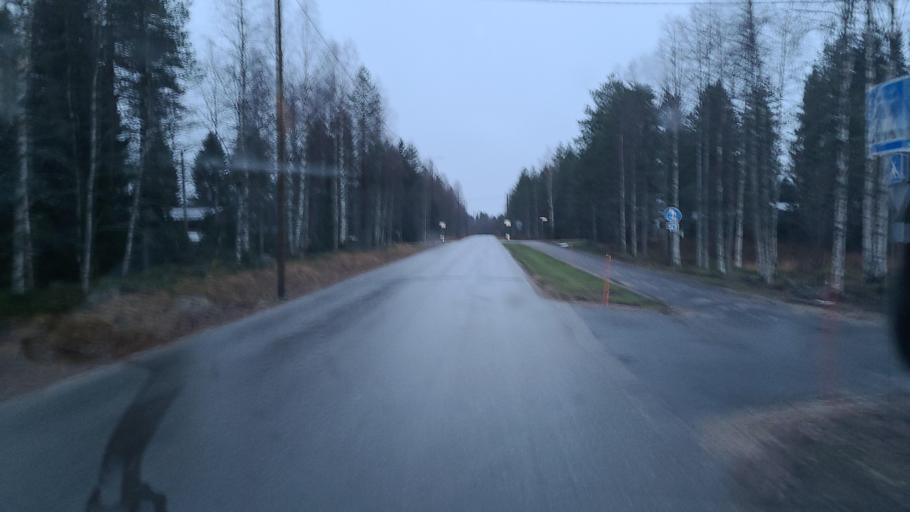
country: FI
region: Lapland
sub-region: Rovaniemi
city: Ranua
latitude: 65.9283
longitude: 26.4939
